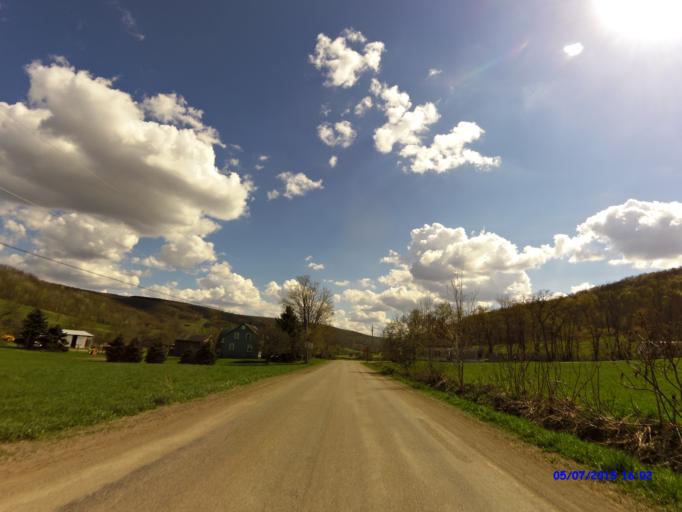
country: US
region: New York
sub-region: Cattaraugus County
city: Franklinville
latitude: 42.2872
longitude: -78.6087
